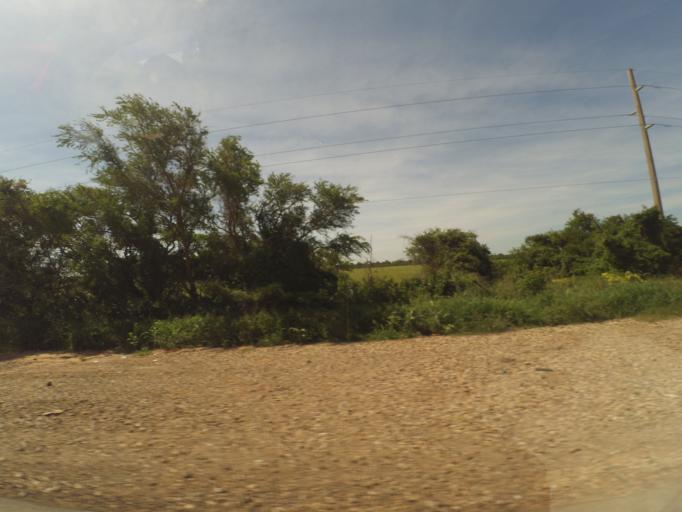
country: BO
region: Santa Cruz
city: San Julian
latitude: -17.7218
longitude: -62.9082
